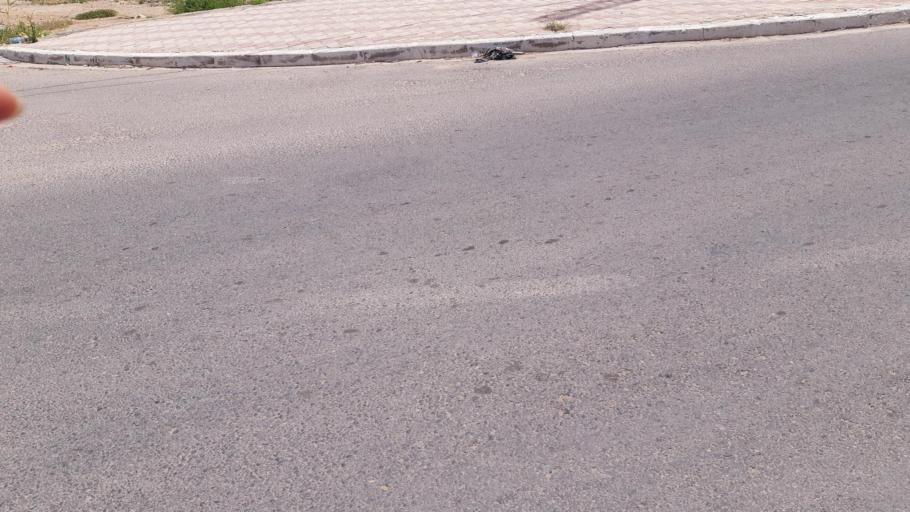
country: TN
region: Qabis
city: Gabes
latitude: 33.8795
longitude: 10.1166
